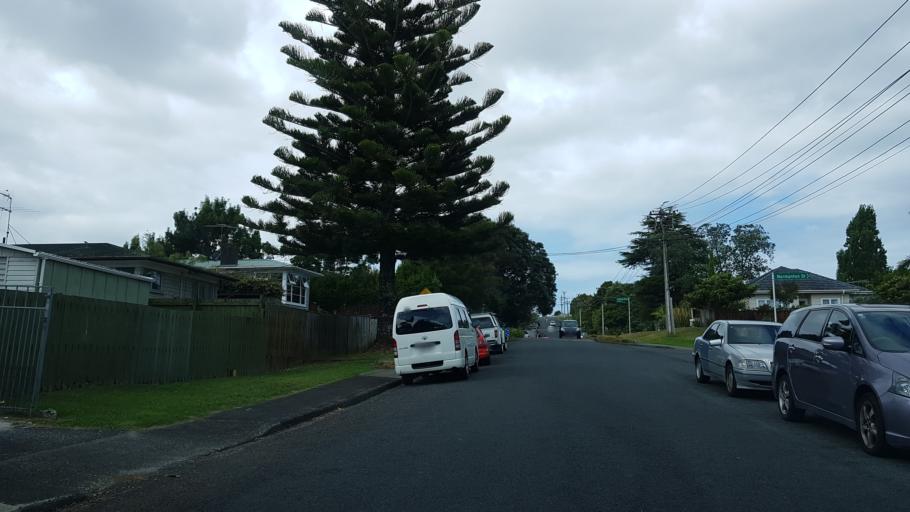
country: NZ
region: Auckland
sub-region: Auckland
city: North Shore
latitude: -36.7717
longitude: 174.7247
